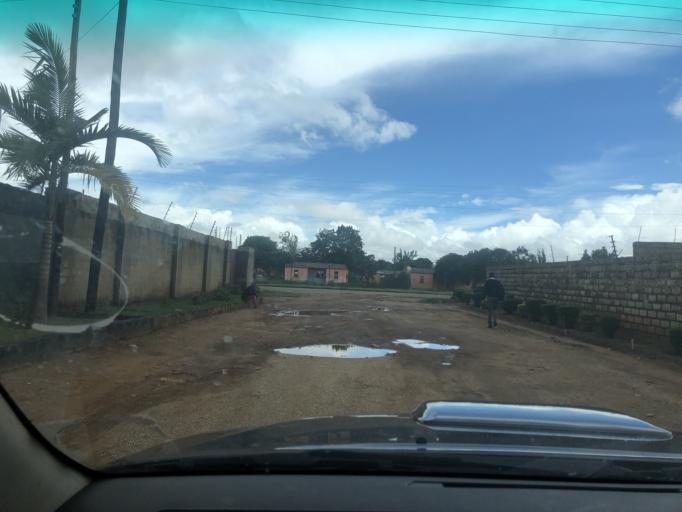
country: ZM
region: Lusaka
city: Lusaka
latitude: -15.4314
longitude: 28.3069
